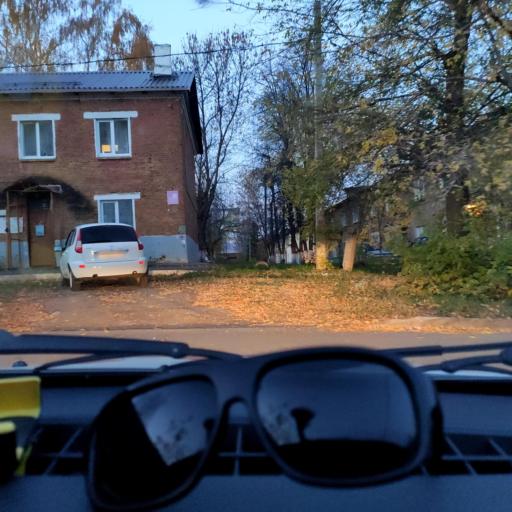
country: RU
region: Bashkortostan
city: Ufa
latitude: 54.7227
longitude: 56.0112
